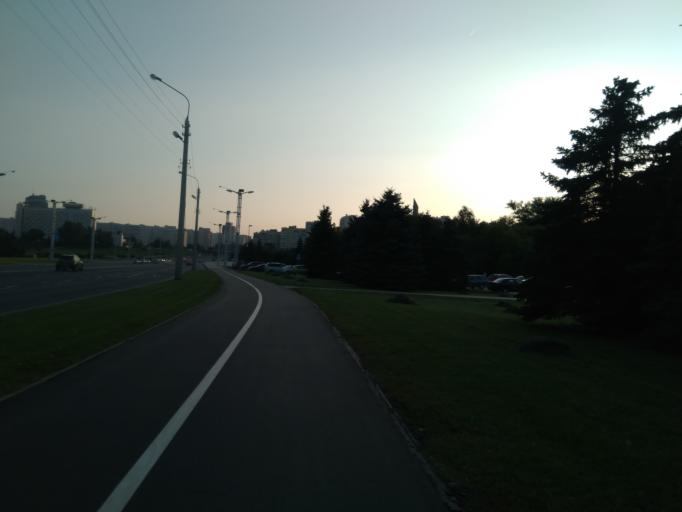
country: BY
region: Minsk
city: Minsk
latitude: 53.9171
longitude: 27.5444
